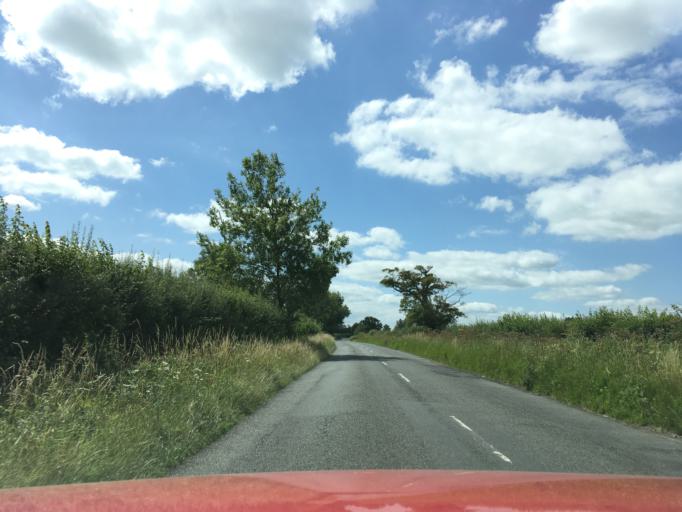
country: GB
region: England
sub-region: Buckinghamshire
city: Winslow
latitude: 51.9247
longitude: -0.8375
